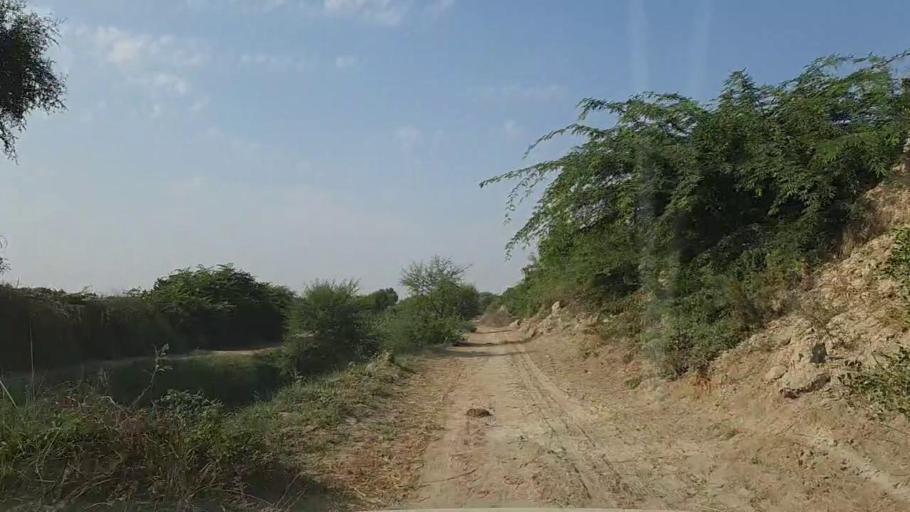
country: PK
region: Sindh
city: Mirpur Batoro
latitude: 24.7096
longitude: 68.2984
